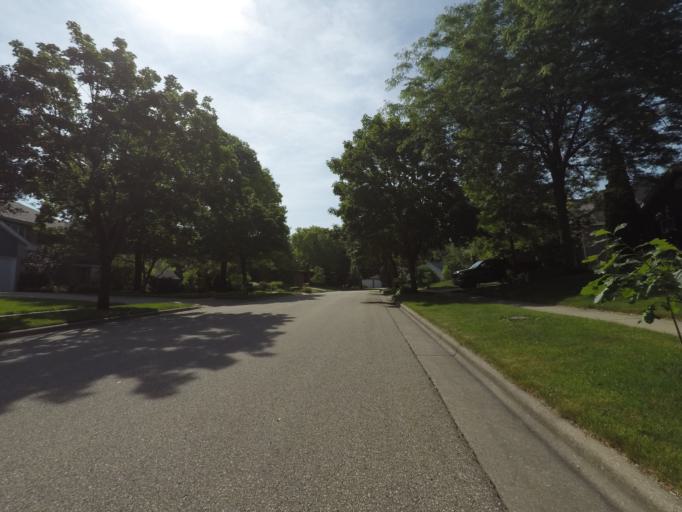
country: US
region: Wisconsin
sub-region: Dane County
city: Middleton
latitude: 43.0796
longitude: -89.4937
